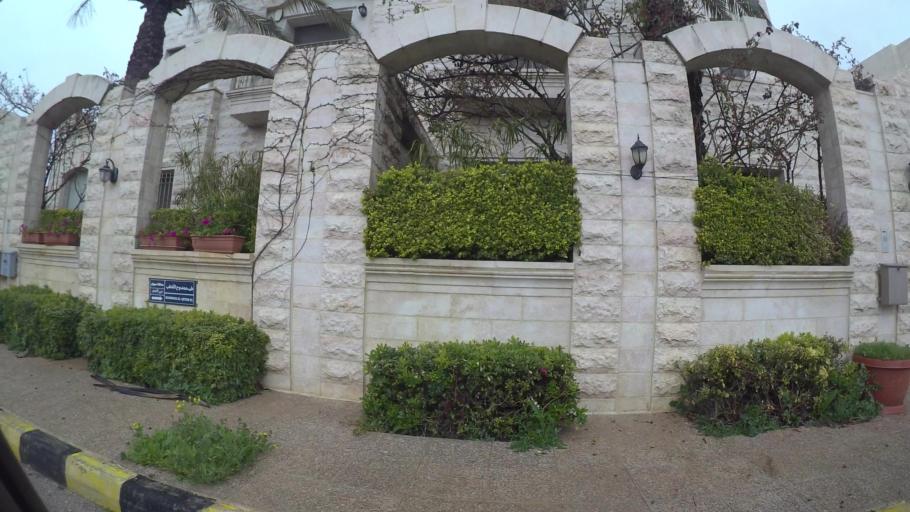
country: JO
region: Amman
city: Al Jubayhah
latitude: 32.0110
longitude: 35.8251
